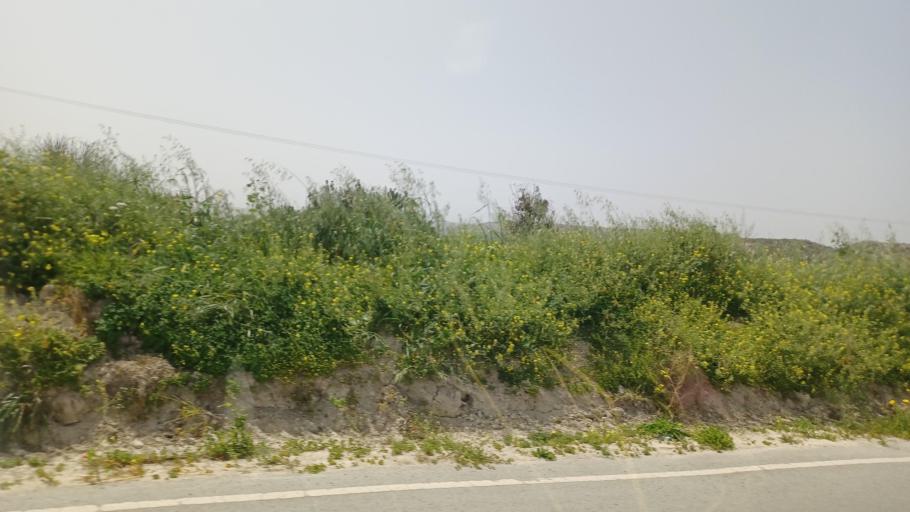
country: CY
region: Limassol
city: Pissouri
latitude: 34.7023
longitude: 32.7503
